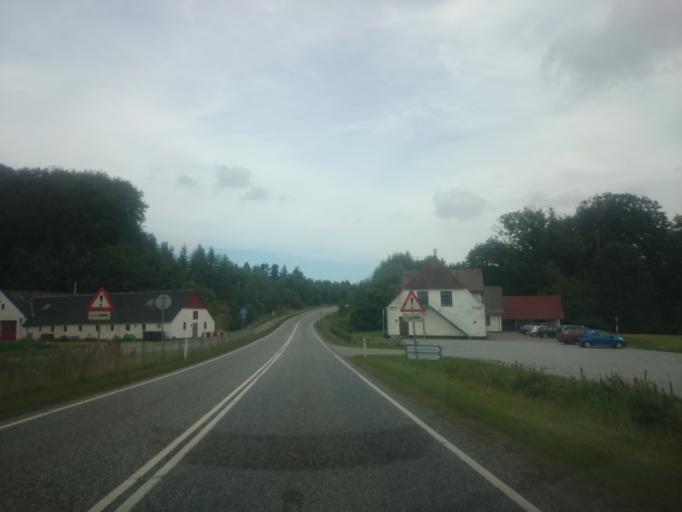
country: DK
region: South Denmark
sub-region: Vejle Kommune
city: Jelling
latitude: 55.6769
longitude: 9.3816
